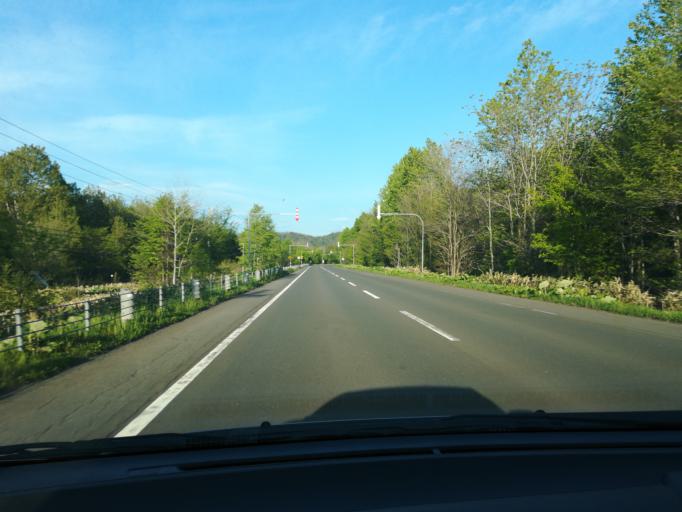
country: JP
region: Hokkaido
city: Shimo-furano
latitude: 43.1355
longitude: 142.6417
